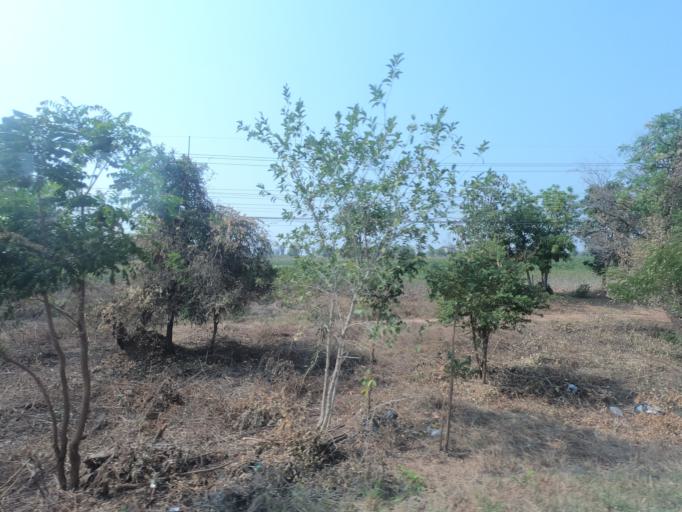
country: TH
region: Nakhon Ratchasima
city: Non Daeng
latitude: 15.3926
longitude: 102.4686
